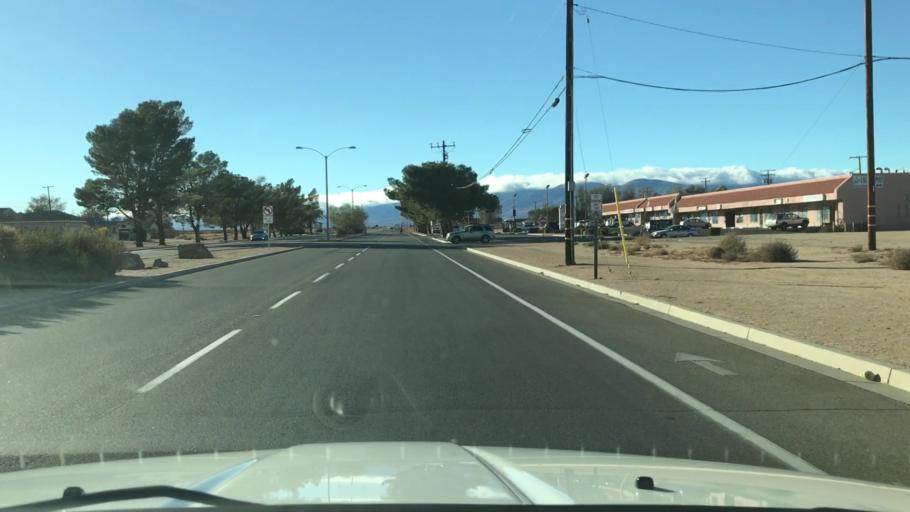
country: US
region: California
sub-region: Kern County
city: California City
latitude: 35.1258
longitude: -118.0003
